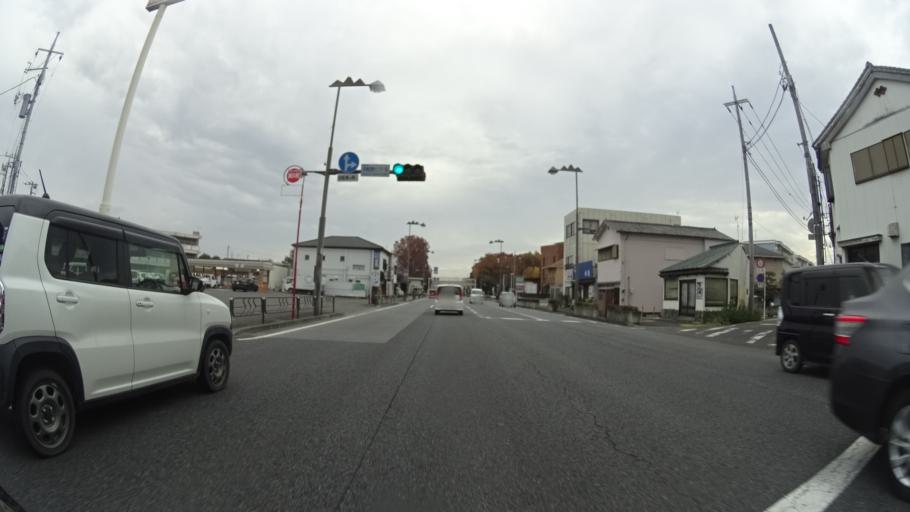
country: JP
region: Gunma
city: Maebashi-shi
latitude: 36.3833
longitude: 139.0913
